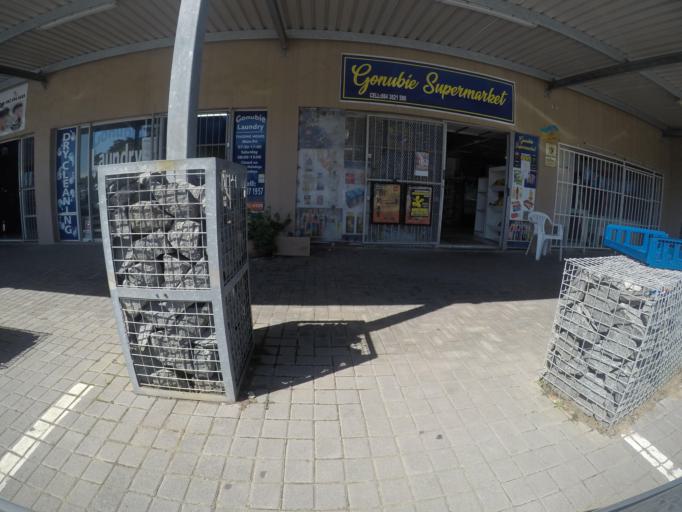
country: ZA
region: Eastern Cape
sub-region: Buffalo City Metropolitan Municipality
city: East London
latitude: -32.9381
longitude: 28.0089
